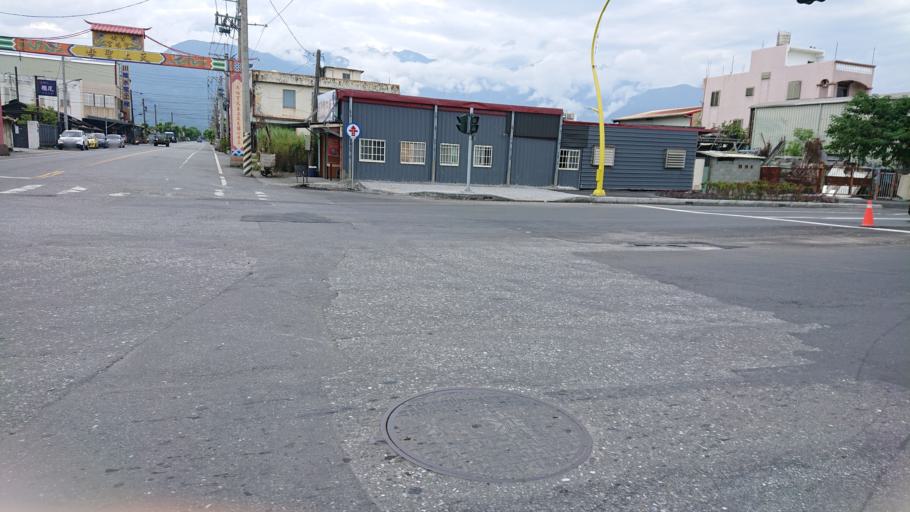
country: TW
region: Taiwan
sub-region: Hualien
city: Hualian
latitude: 23.9496
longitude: 121.5989
